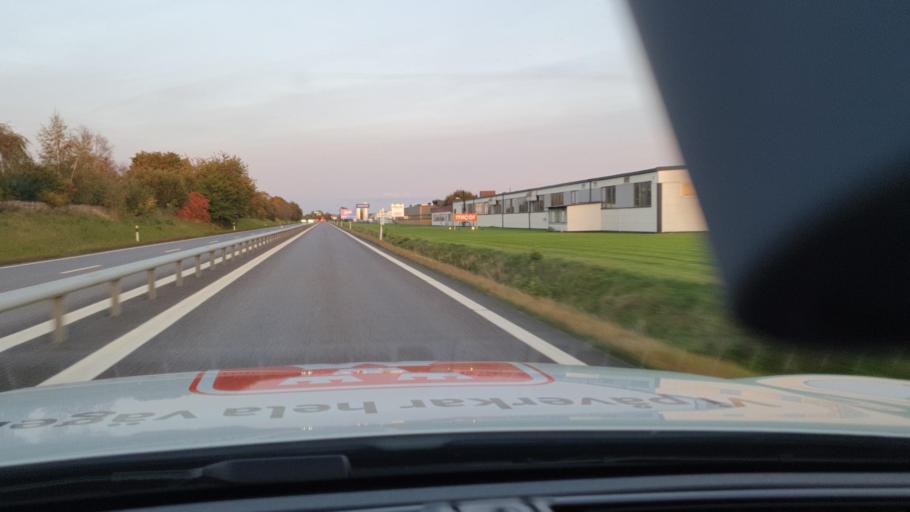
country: SE
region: Halland
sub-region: Laholms Kommun
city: Laholm
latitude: 56.5015
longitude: 13.0241
